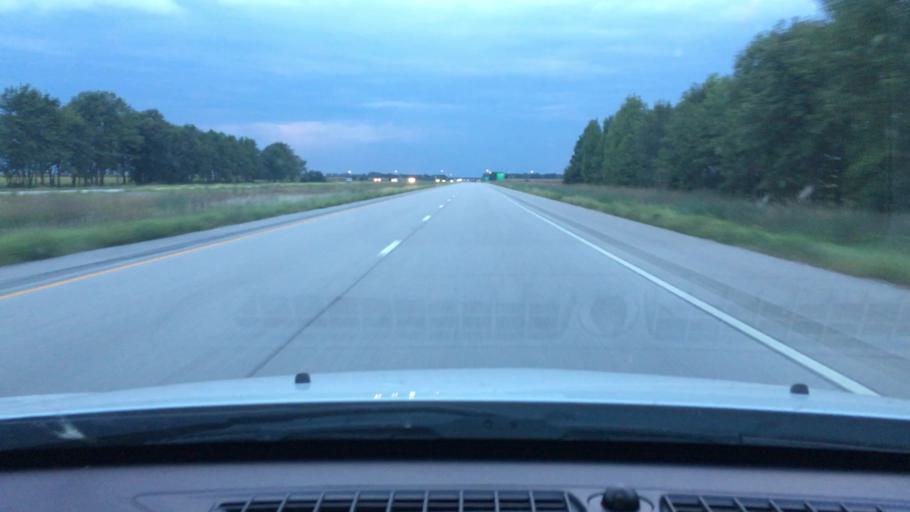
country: US
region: Illinois
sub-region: Sangamon County
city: New Berlin
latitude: 39.7371
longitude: -90.0218
